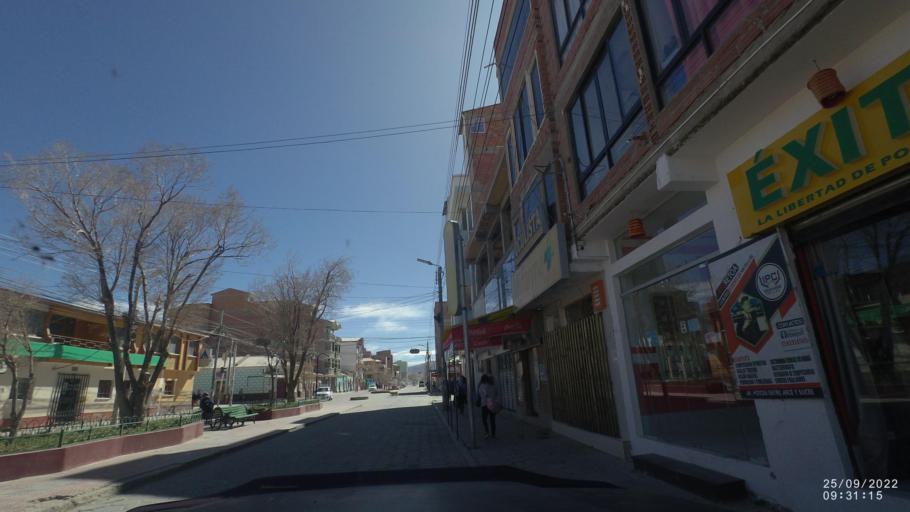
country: BO
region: Potosi
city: Uyuni
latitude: -20.4621
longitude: -66.8236
